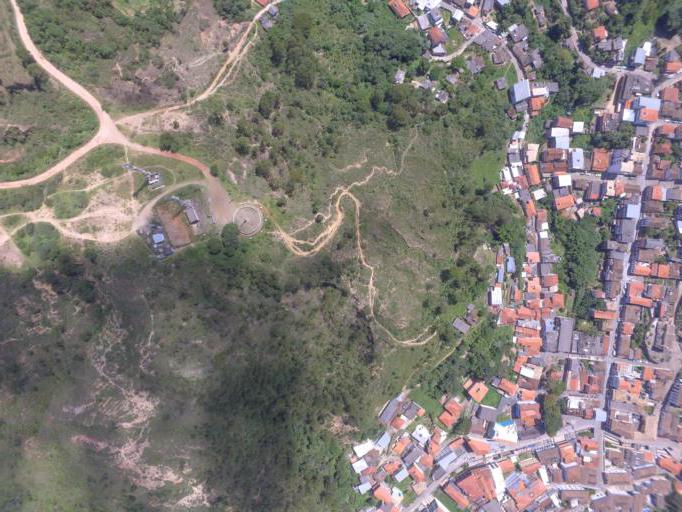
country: BR
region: Minas Gerais
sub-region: Tiradentes
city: Tiradentes
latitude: -21.0547
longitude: -44.0787
